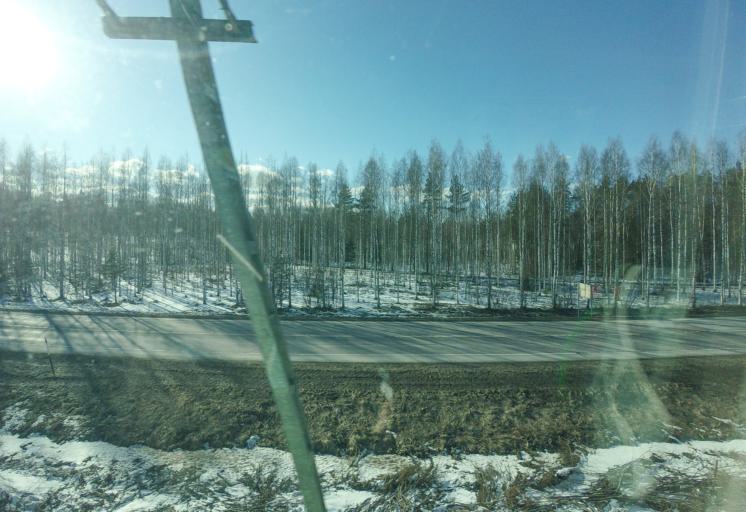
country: FI
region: South Karelia
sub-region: Imatra
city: Parikkala
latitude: 61.5250
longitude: 29.5157
